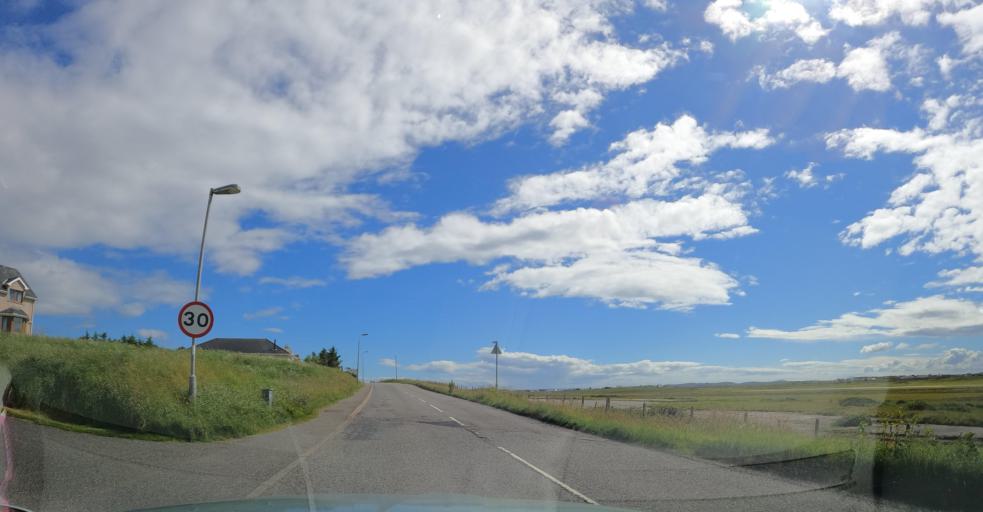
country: GB
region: Scotland
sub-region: Eilean Siar
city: Stornoway
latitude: 58.2093
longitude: -6.3231
